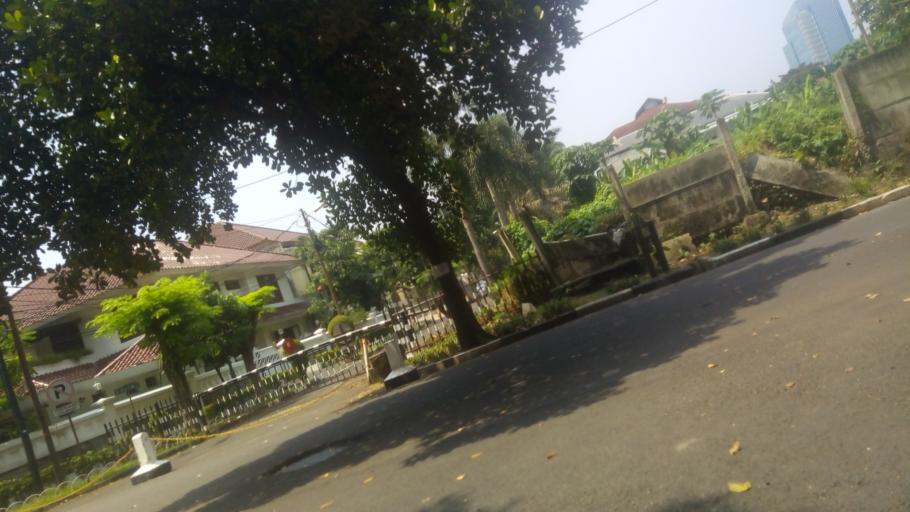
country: ID
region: Jakarta Raya
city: Jakarta
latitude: -6.2357
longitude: 106.8305
